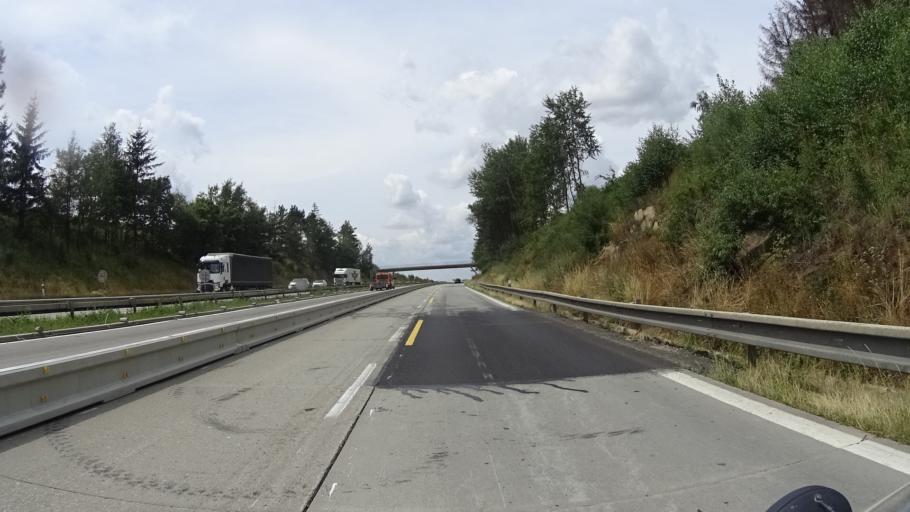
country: CZ
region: Vysocina
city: Kamenice
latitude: 49.4073
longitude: 15.7848
